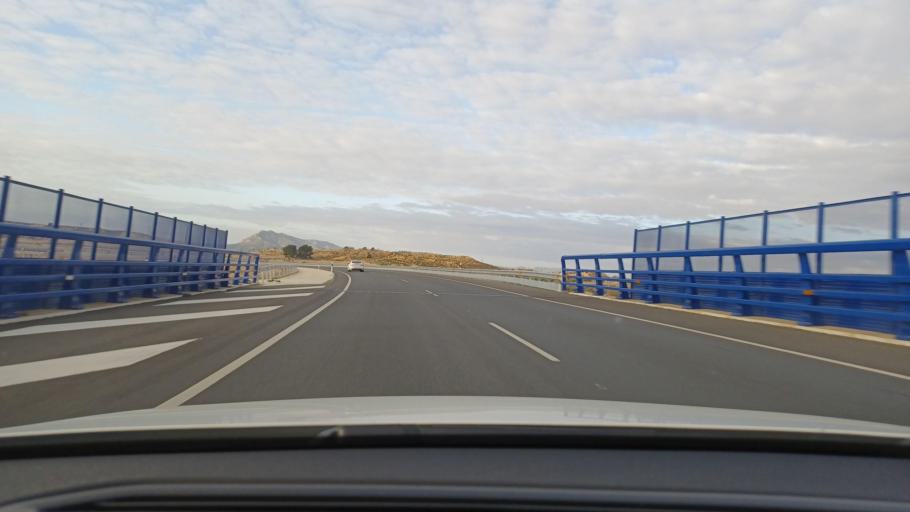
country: ES
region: Castille-La Mancha
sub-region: Provincia de Albacete
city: Caudete
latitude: 38.7293
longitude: -0.9361
